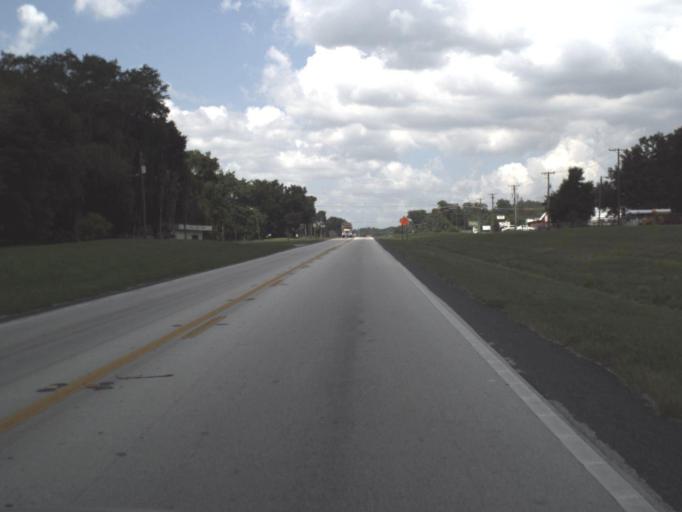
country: US
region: Florida
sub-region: Hillsborough County
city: Thonotosassa
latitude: 28.0568
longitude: -82.3152
